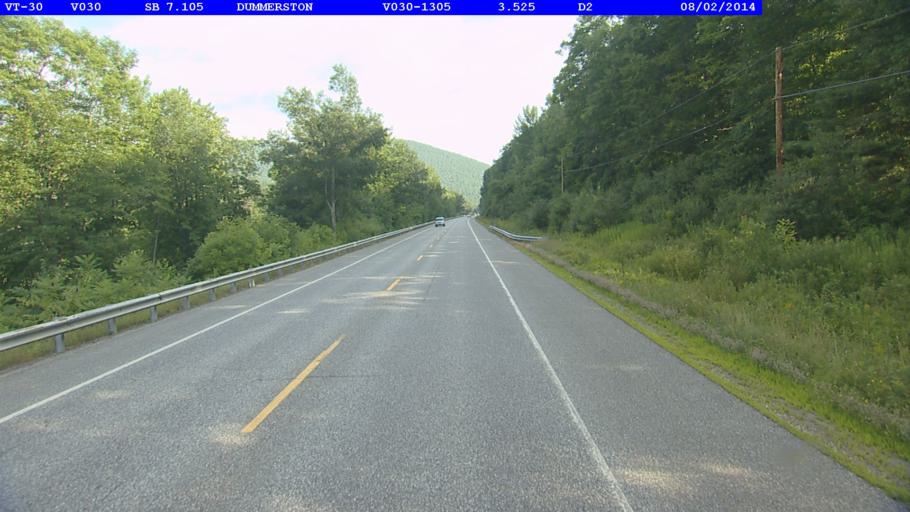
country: US
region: Vermont
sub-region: Windham County
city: Newfane
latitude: 42.9427
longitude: -72.6164
